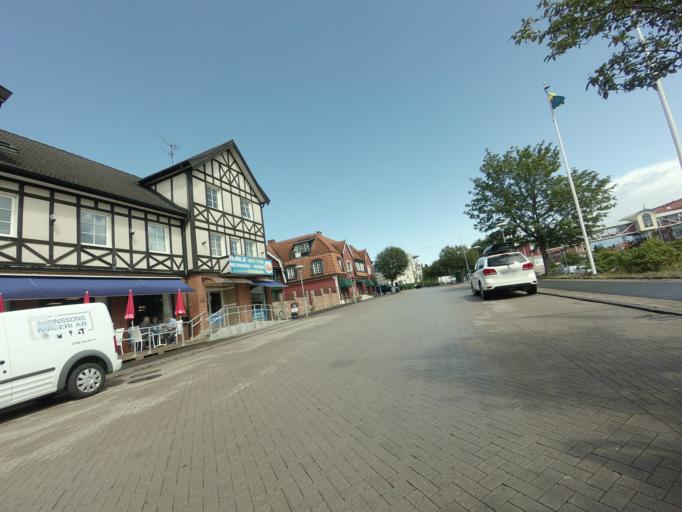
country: SE
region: Skane
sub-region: Osby Kommun
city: Osby
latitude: 56.3809
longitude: 13.9943
